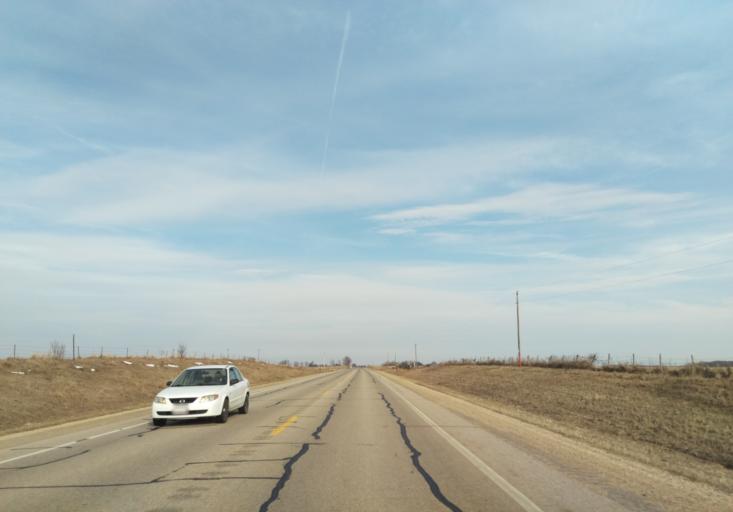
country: US
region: Wisconsin
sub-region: Grant County
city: Fennimore
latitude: 42.9736
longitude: -90.5215
